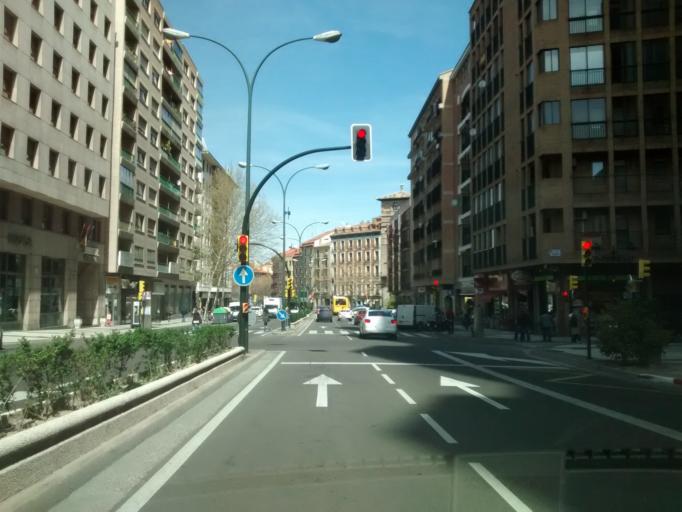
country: ES
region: Aragon
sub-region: Provincia de Zaragoza
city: Zaragoza
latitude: 41.6528
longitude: -0.8846
